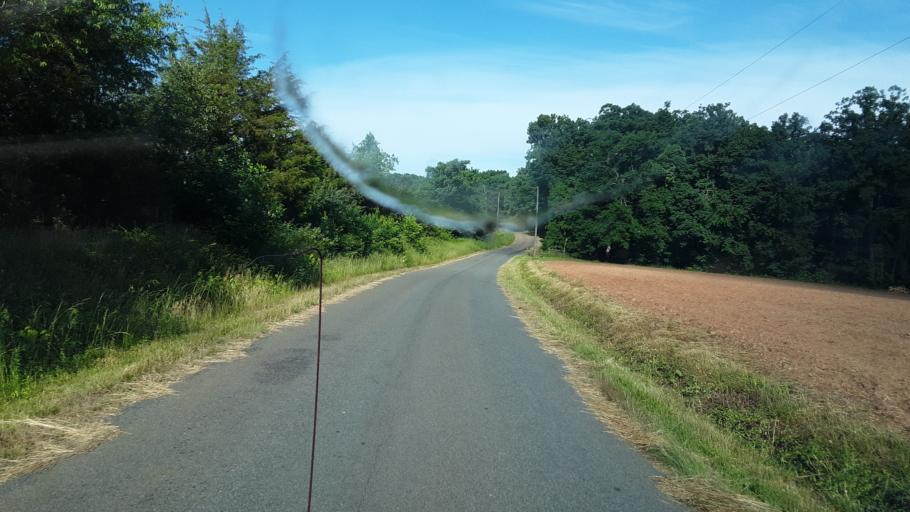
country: US
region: Virginia
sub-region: Pittsylvania County
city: Chatham
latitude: 36.8391
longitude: -79.4035
